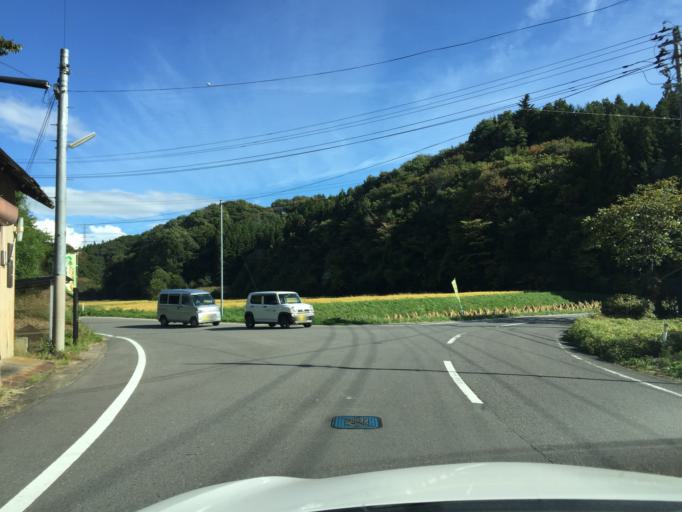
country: JP
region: Fukushima
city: Ishikawa
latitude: 37.2159
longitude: 140.5810
